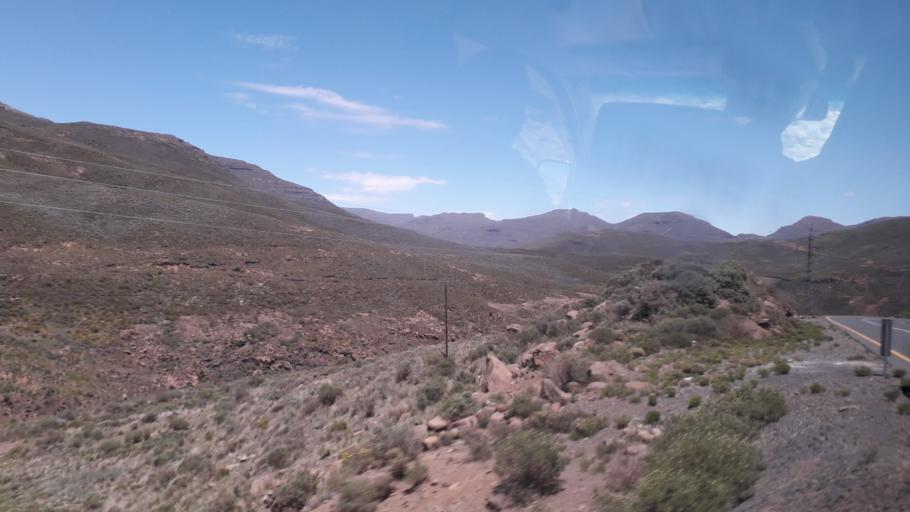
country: ZA
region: Orange Free State
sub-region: Thabo Mofutsanyana District Municipality
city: Phuthaditjhaba
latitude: -28.7665
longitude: 28.6600
